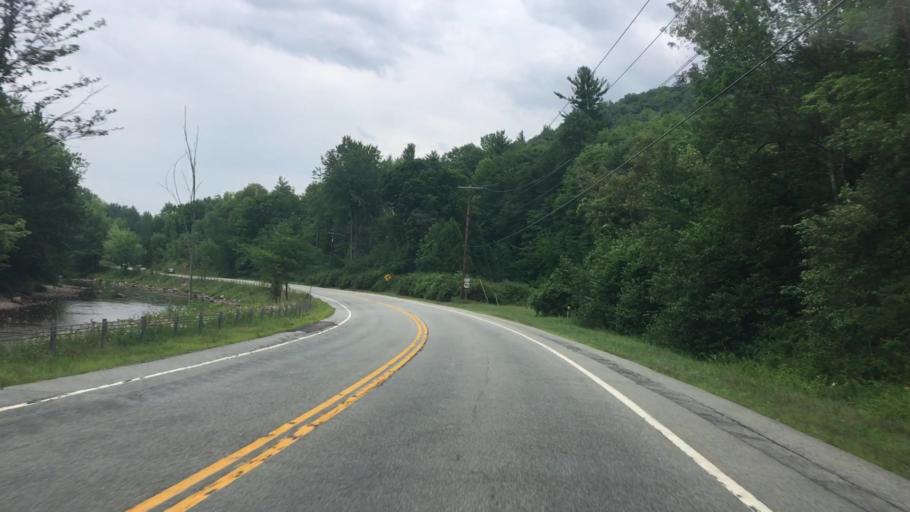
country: US
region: New York
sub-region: Essex County
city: Lake Placid
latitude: 44.2754
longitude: -73.7902
